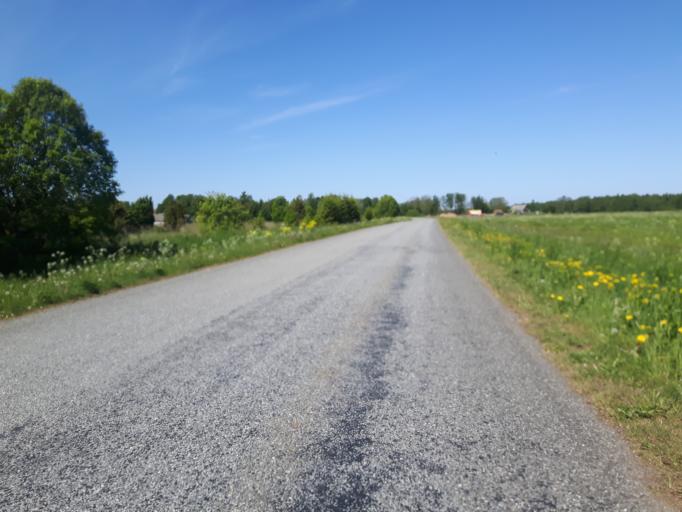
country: EE
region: Ida-Virumaa
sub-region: Aseri vald
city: Aseri
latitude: 59.4732
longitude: 26.8027
